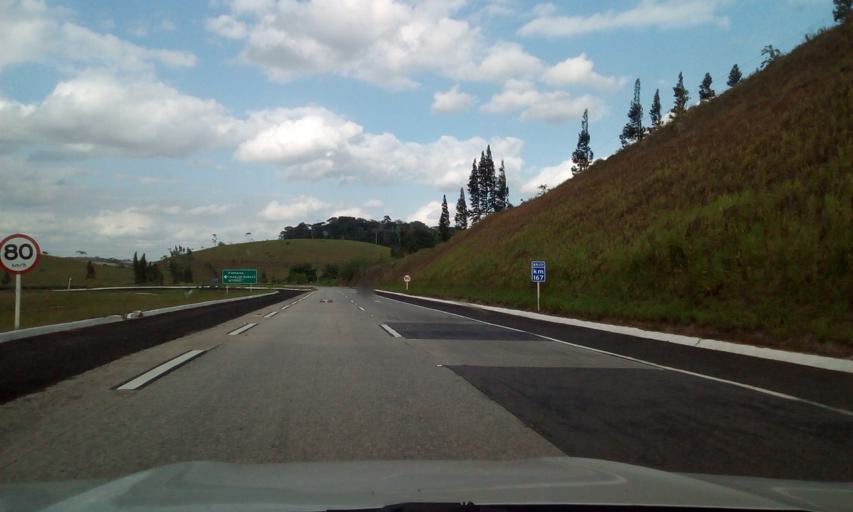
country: BR
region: Pernambuco
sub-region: Joaquim Nabuco
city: Joaquim Nabuco
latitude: -8.5719
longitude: -35.4791
